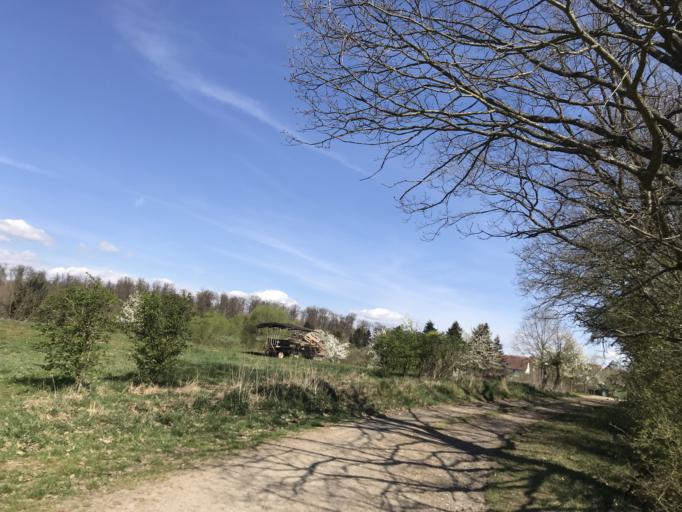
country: DE
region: Hesse
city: Beuern
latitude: 50.6566
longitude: 8.8095
